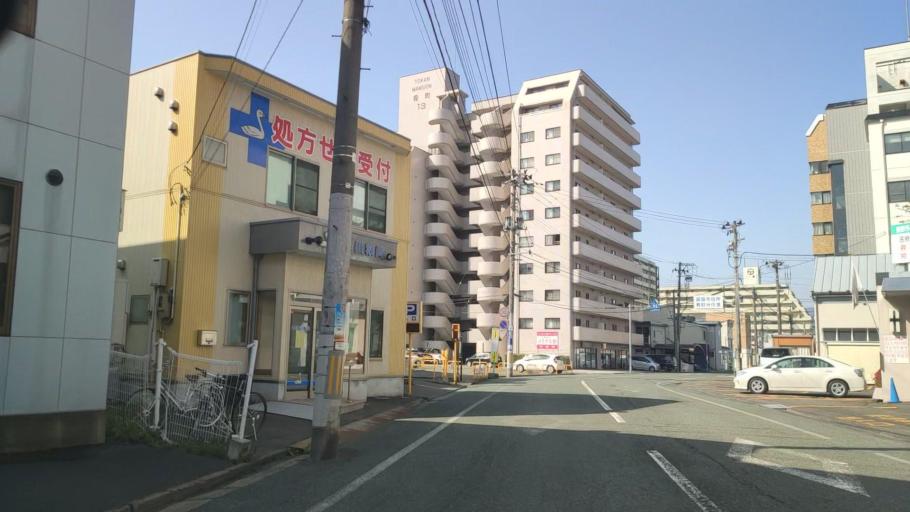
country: JP
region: Iwate
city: Morioka-shi
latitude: 39.6983
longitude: 141.1535
